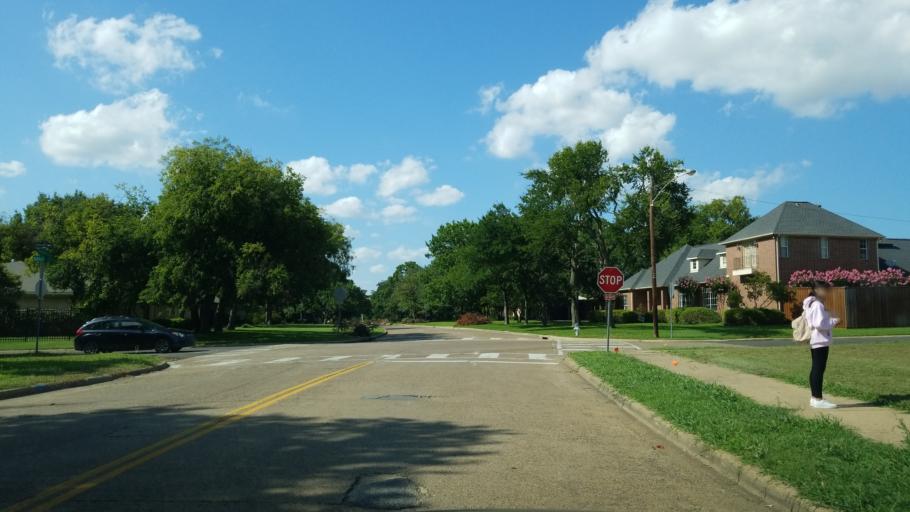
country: US
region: Texas
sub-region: Dallas County
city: University Park
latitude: 32.8832
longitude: -96.8488
